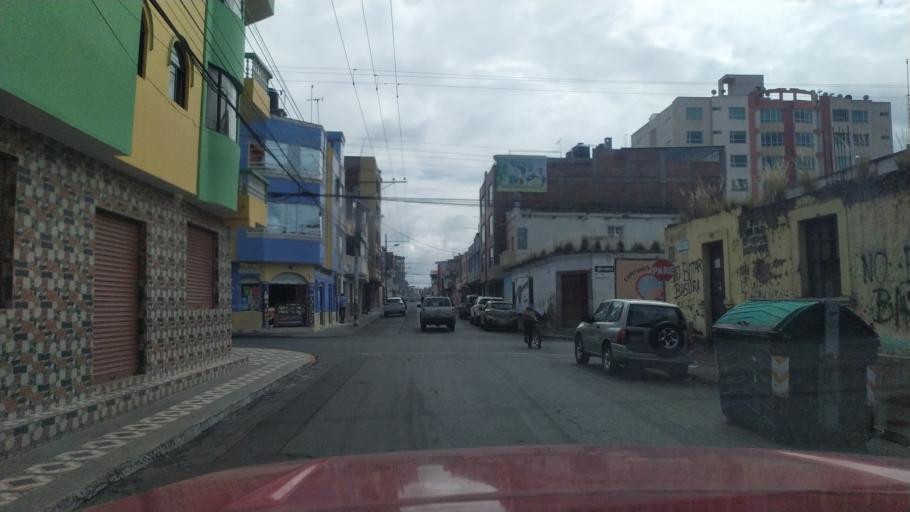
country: EC
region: Chimborazo
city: Riobamba
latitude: -1.6687
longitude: -78.6493
